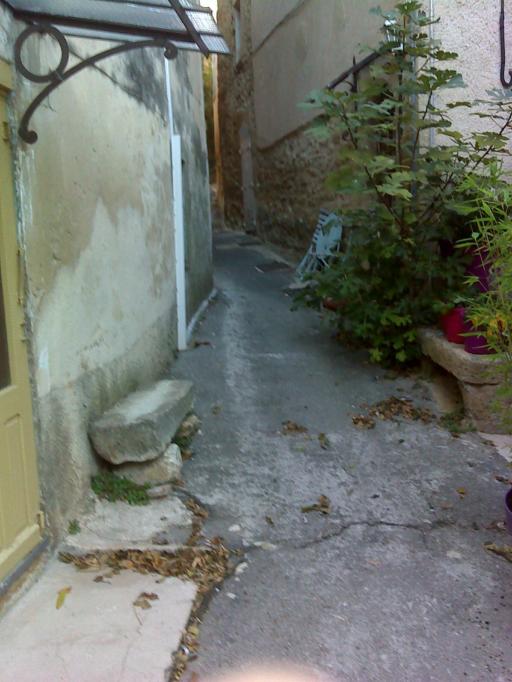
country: FR
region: Provence-Alpes-Cote d'Azur
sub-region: Departement du Vaucluse
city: Lourmarin
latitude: 43.7628
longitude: 5.3628
